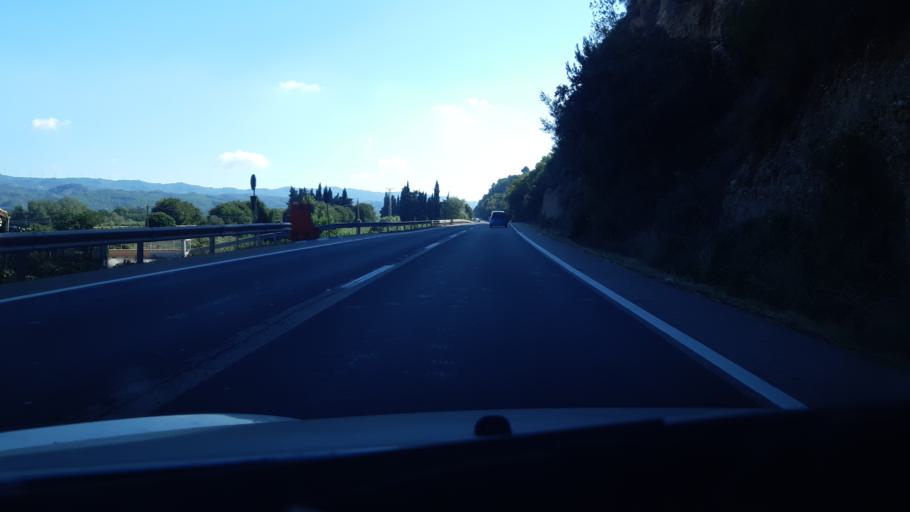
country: ES
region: Catalonia
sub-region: Provincia de Tarragona
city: Tivenys
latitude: 40.8677
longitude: 0.5040
